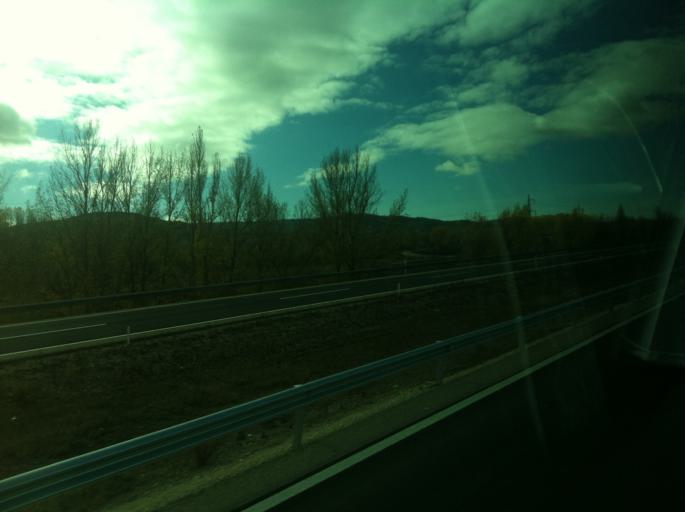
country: ES
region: Castille and Leon
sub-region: Provincia de Burgos
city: Castil de Peones
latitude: 42.4862
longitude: -3.3904
